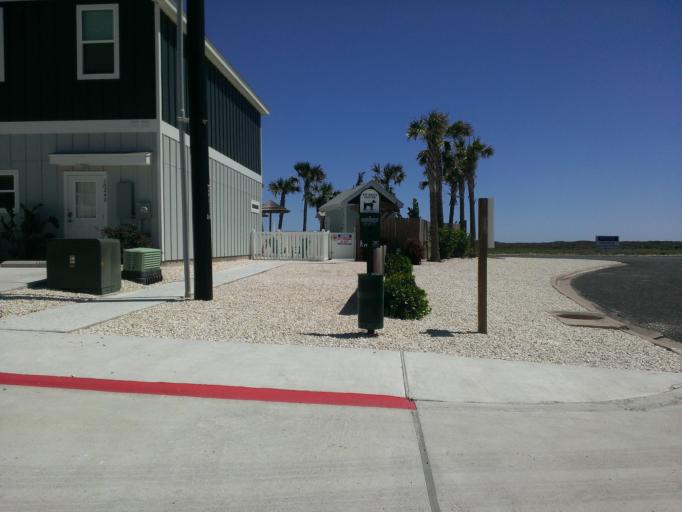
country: US
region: Texas
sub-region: Nueces County
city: Corpus Christi
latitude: 27.6038
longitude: -97.2112
